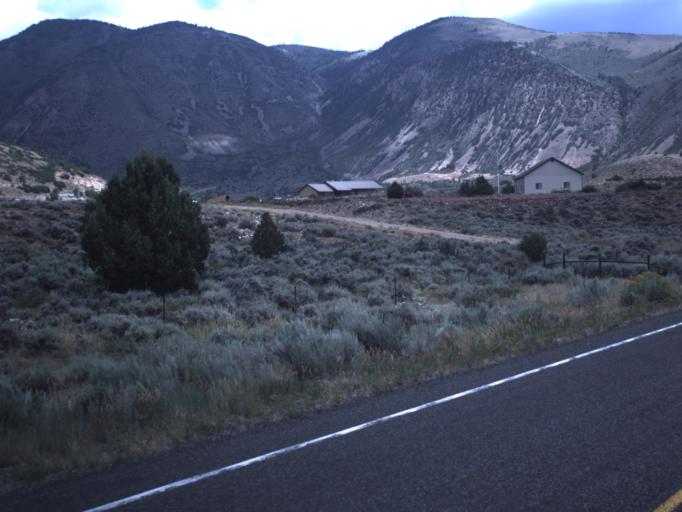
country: US
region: Utah
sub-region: Summit County
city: Francis
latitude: 40.4625
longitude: -110.8373
